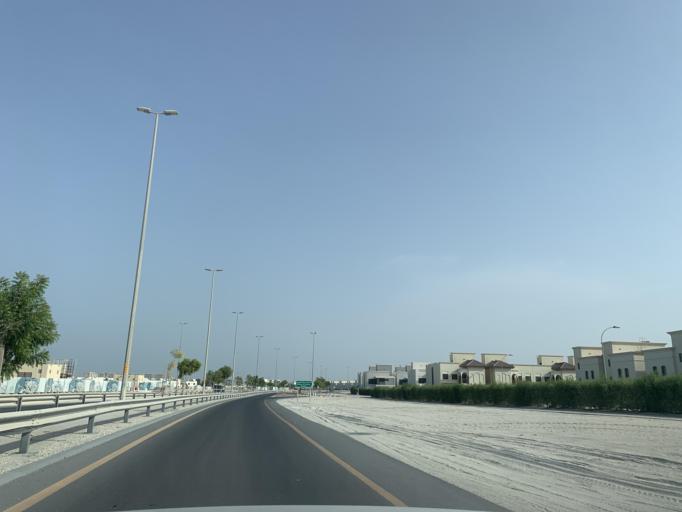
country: BH
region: Muharraq
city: Al Muharraq
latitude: 26.3191
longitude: 50.6306
